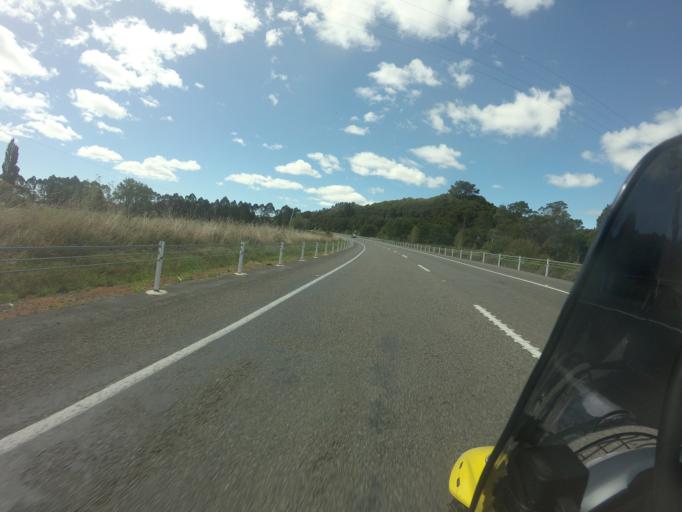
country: NZ
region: Bay of Plenty
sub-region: Whakatane District
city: Edgecumbe
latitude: -38.0208
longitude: 176.8497
